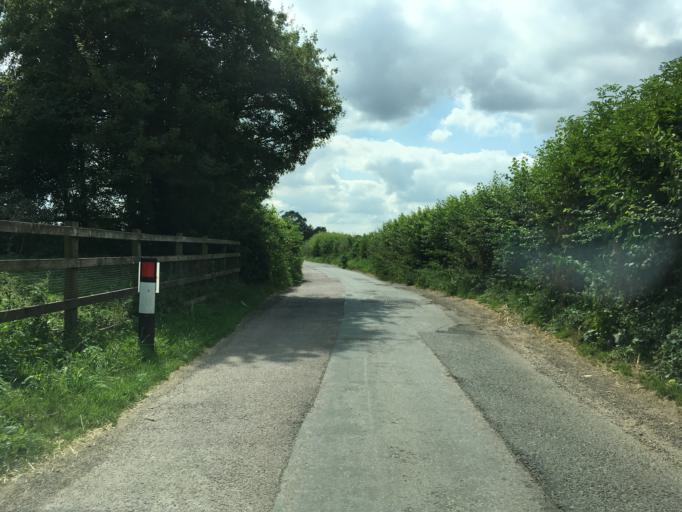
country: GB
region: England
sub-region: Gloucestershire
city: Gloucester
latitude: 51.9037
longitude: -2.2509
